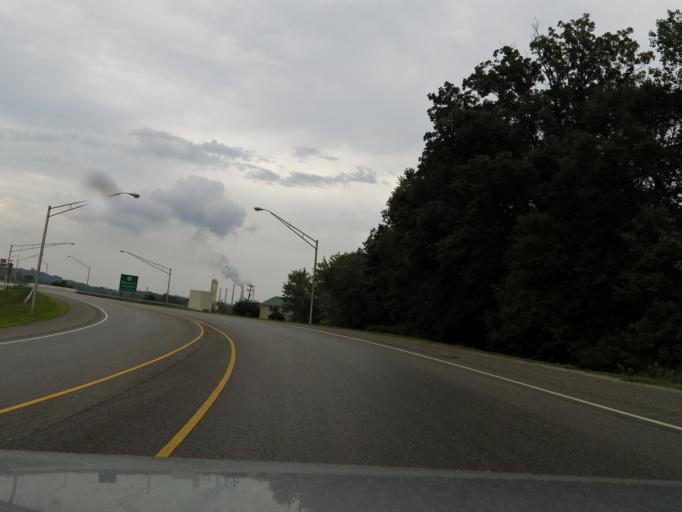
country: US
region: Ohio
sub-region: Brown County
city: Aberdeen
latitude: 38.6858
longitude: -83.7743
